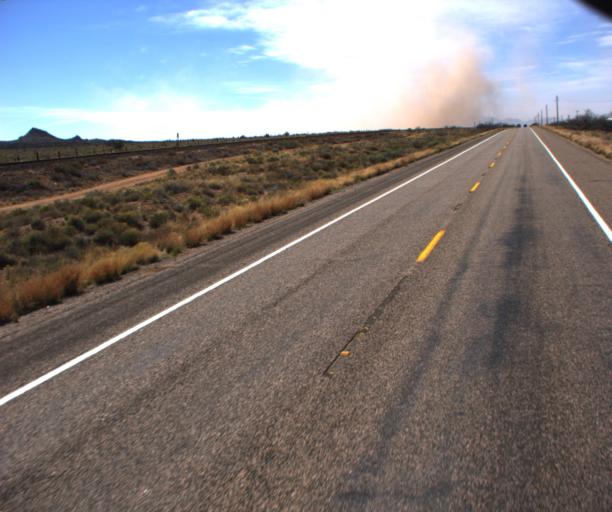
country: US
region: Arizona
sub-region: Mohave County
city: New Kingman-Butler
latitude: 35.4106
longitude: -113.7780
